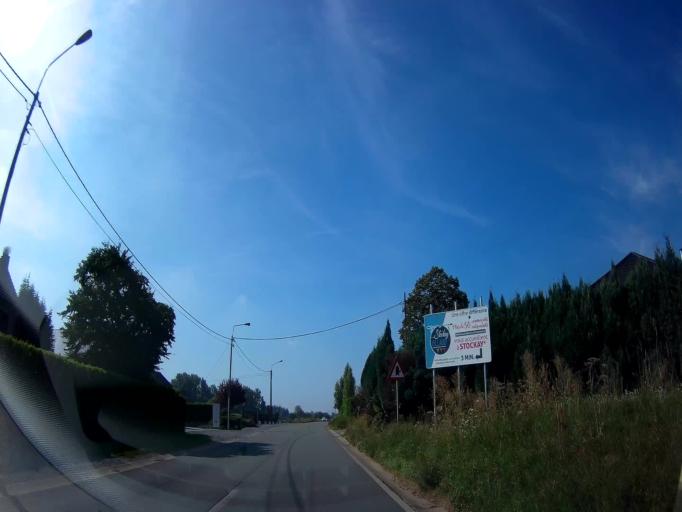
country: BE
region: Wallonia
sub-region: Province de Liege
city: Verlaine
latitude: 50.5987
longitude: 5.3438
